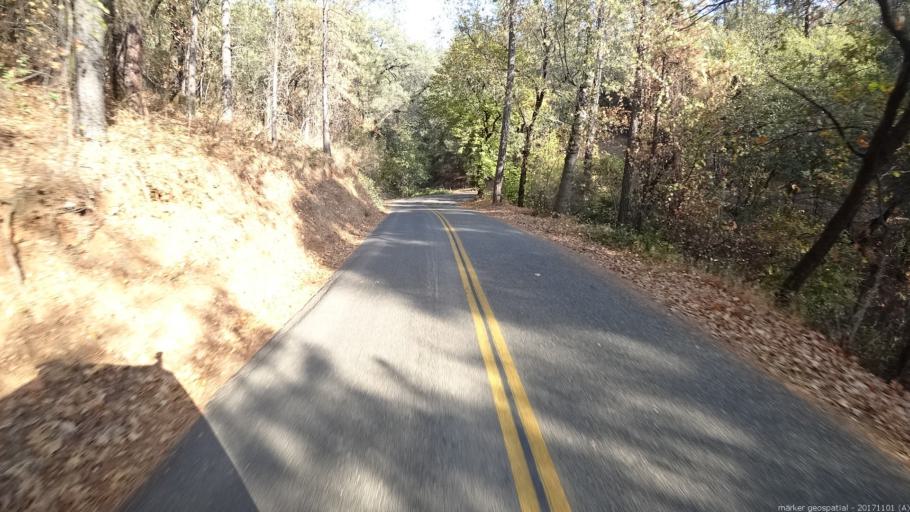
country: US
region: California
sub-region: Shasta County
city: Shasta Lake
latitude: 40.8039
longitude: -122.3122
